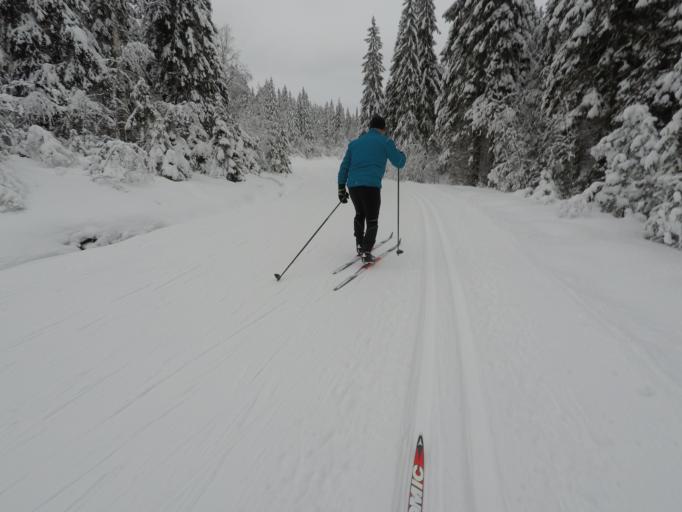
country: SE
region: Dalarna
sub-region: Ludvika Kommun
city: Abborrberget
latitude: 60.1478
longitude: 14.4844
